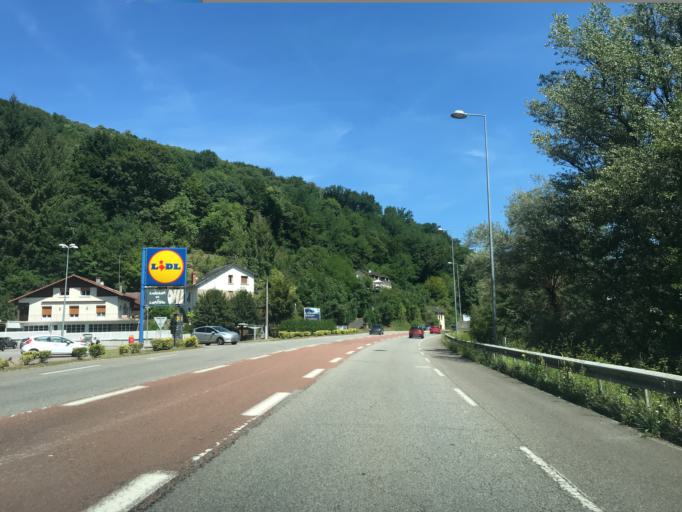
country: FR
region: Limousin
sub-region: Departement de la Correze
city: Tulle
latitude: 45.2471
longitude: 1.7465
